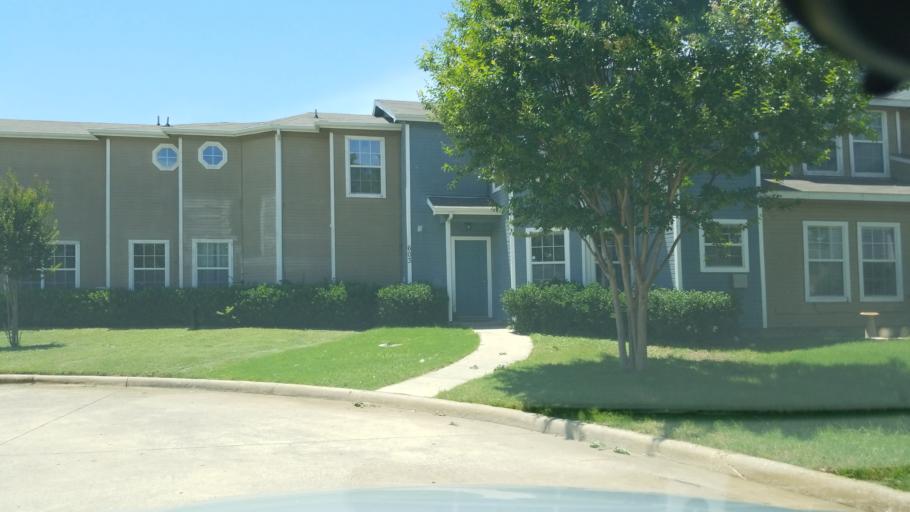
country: US
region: Texas
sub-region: Dallas County
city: Irving
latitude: 32.8213
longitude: -96.9520
